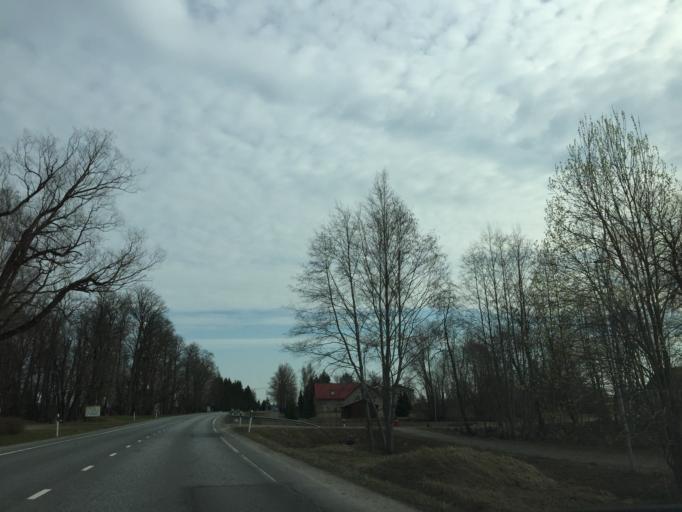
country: EE
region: Ida-Virumaa
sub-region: Johvi vald
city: Johvi
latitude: 59.2725
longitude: 27.5118
